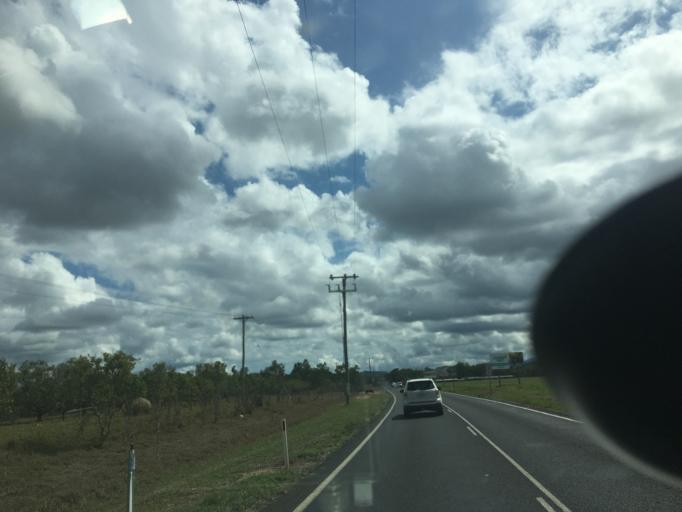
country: AU
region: Queensland
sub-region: Tablelands
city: Mareeba
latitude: -17.0037
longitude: 145.4525
